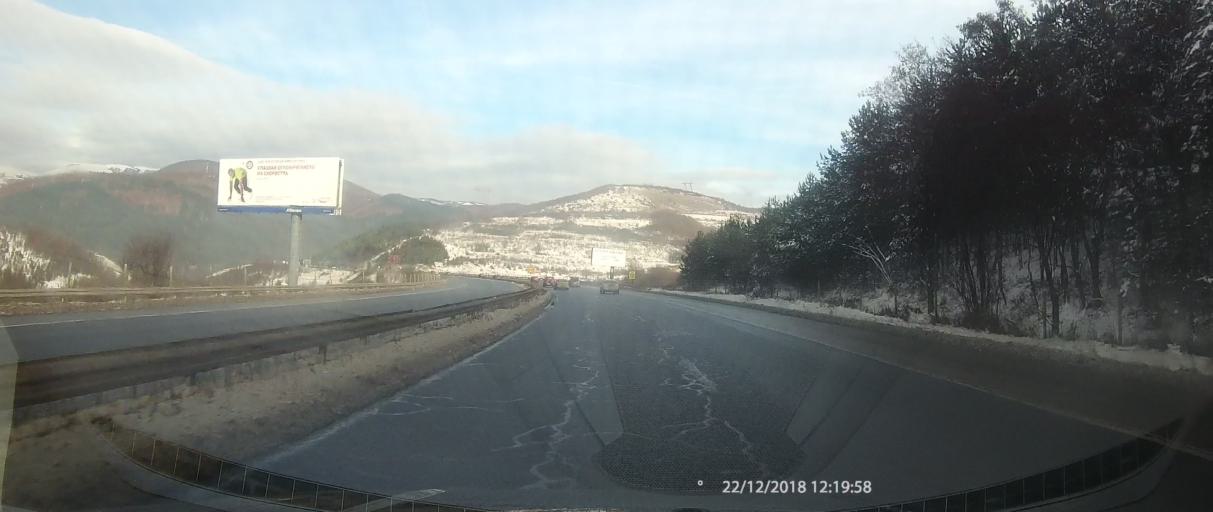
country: BG
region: Sofiya
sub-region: Obshtina Gorna Malina
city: Gorna Malina
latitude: 42.7381
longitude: 23.6576
